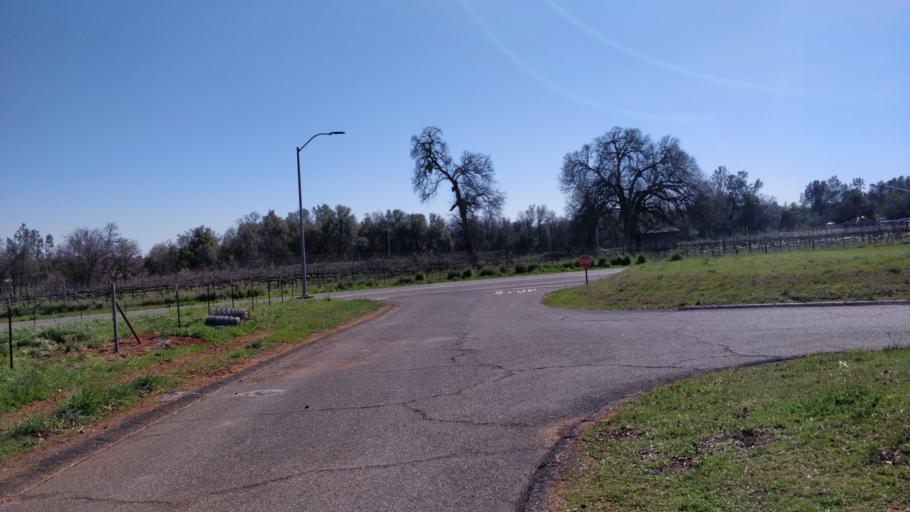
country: US
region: California
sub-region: Shasta County
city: Shasta Lake
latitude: 40.6232
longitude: -122.3150
